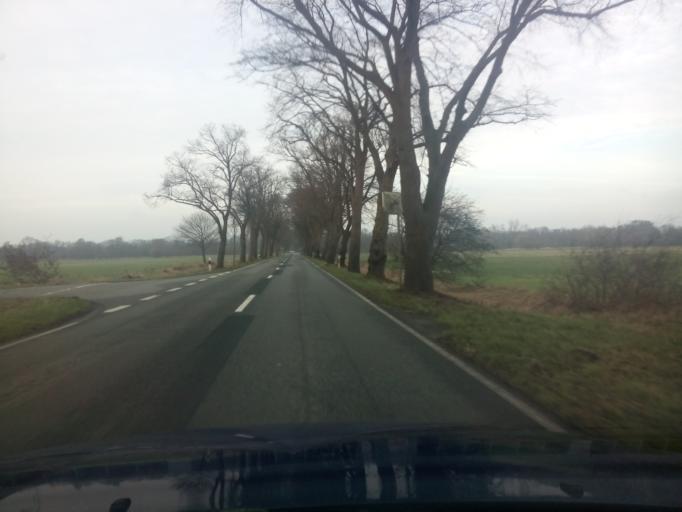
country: DE
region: Lower Saxony
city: Oyten
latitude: 53.1071
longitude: 9.0548
